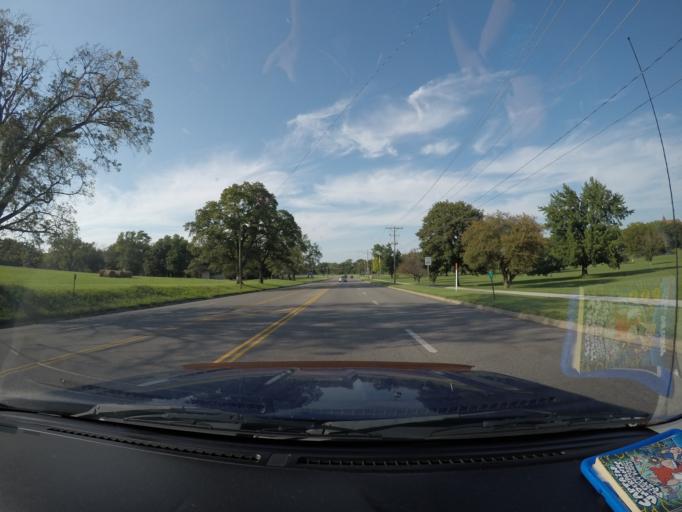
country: US
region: Kansas
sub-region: Leavenworth County
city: Lansing
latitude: 39.2752
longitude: -94.8997
